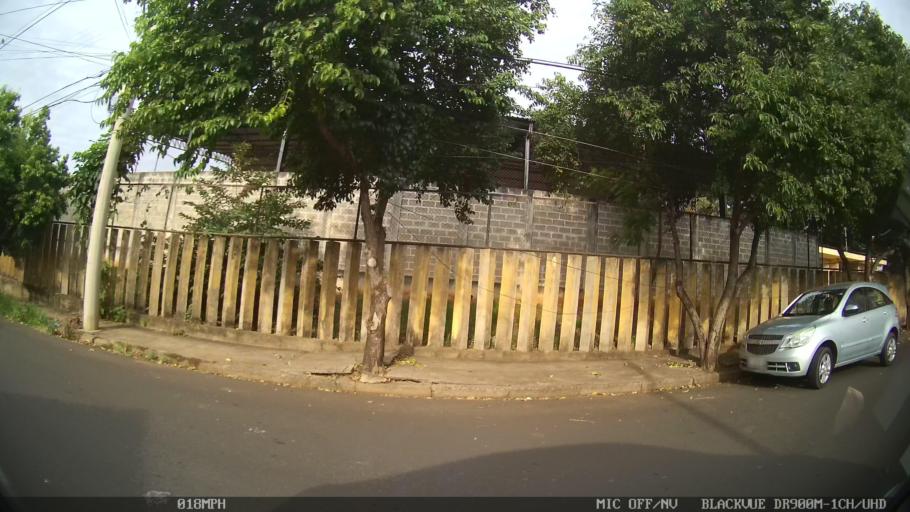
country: BR
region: Sao Paulo
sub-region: Piracicaba
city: Piracicaba
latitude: -22.7346
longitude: -47.6266
